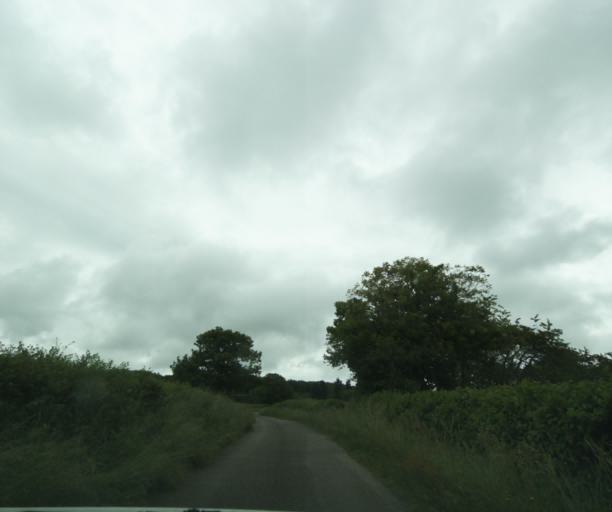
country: FR
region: Bourgogne
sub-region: Departement de Saone-et-Loire
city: Charolles
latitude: 46.4978
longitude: 4.2824
